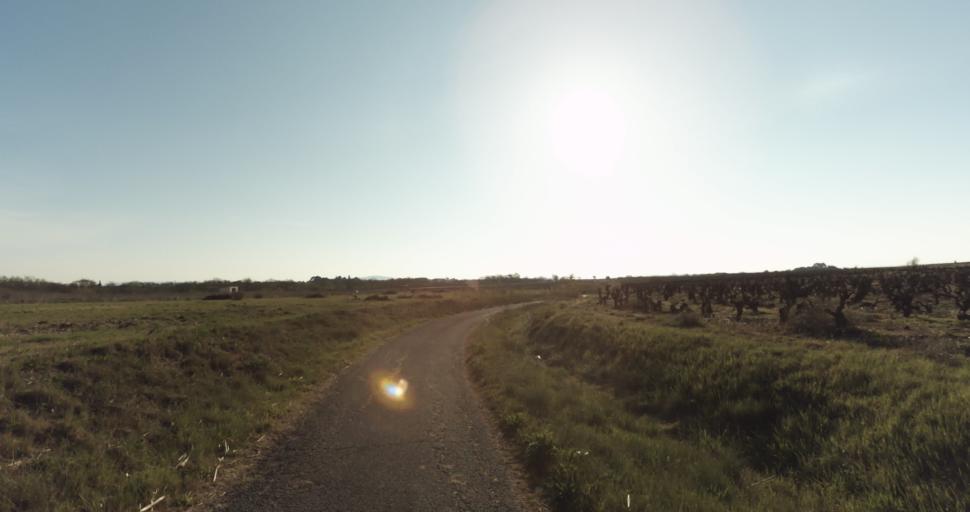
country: FR
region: Languedoc-Roussillon
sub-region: Departement de l'Herault
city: Marseillan
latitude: 43.3830
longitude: 3.5300
